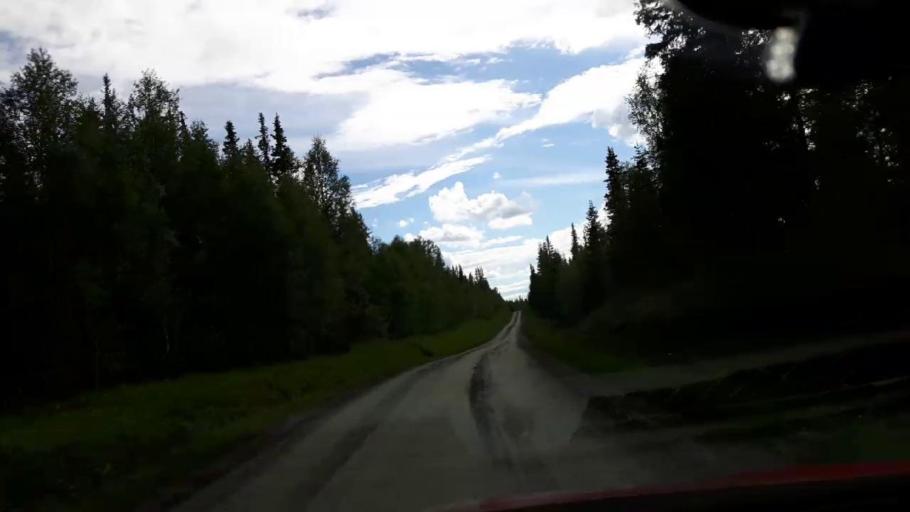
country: SE
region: Jaemtland
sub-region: Krokoms Kommun
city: Valla
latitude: 63.8651
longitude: 14.1143
